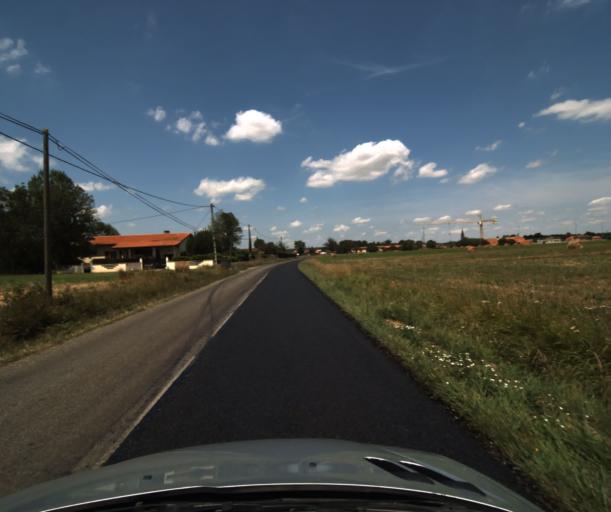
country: FR
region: Midi-Pyrenees
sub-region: Departement de la Haute-Garonne
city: Saint-Lys
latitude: 43.5070
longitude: 1.1837
